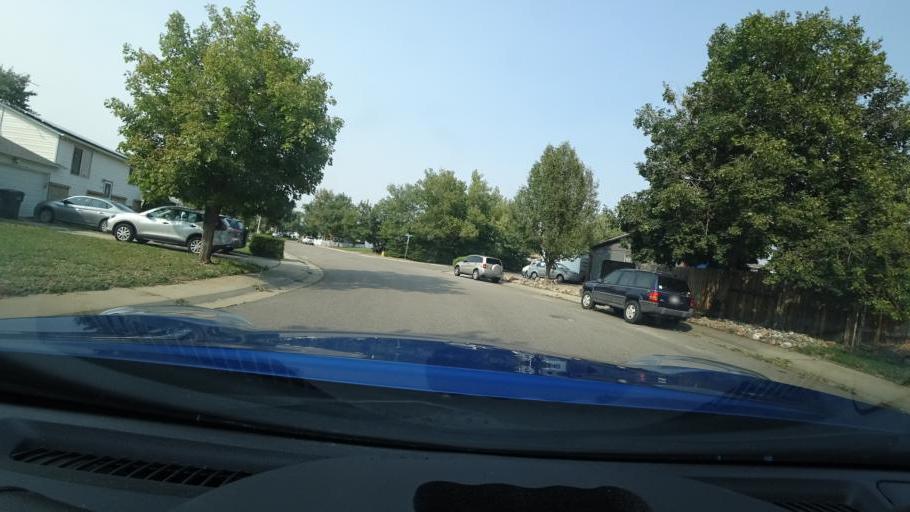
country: US
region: Colorado
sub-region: Adams County
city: Aurora
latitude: 39.6660
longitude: -104.8003
